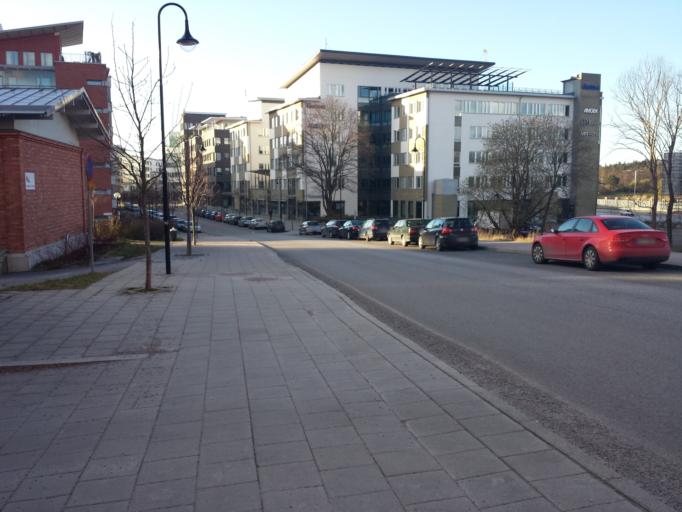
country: SE
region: Stockholm
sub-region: Norrtalje Kommun
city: Bergshamra
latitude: 59.3736
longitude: 18.0157
